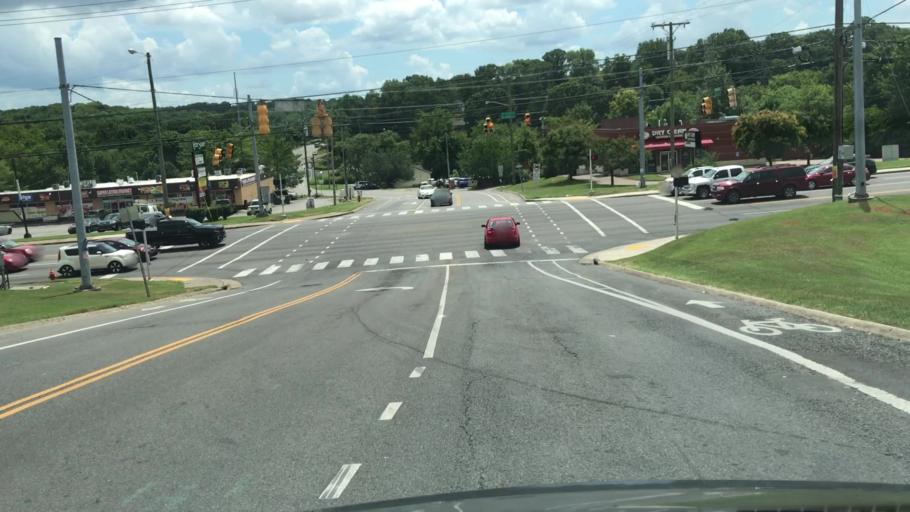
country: US
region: Tennessee
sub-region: Williamson County
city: Brentwood Estates
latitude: 36.0459
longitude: -86.7036
